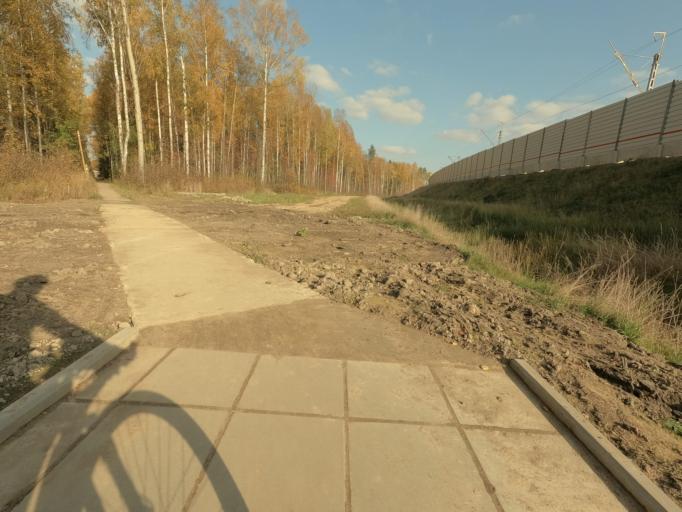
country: RU
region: Leningrad
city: Mga
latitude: 59.7601
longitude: 31.1141
